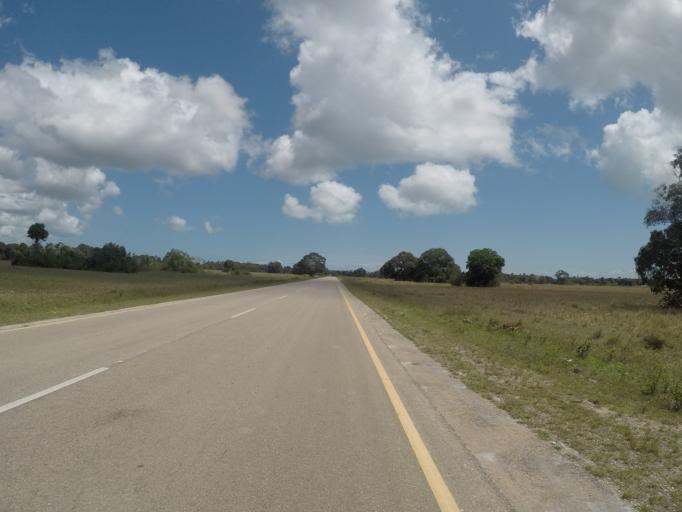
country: TZ
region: Zanzibar Central/South
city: Koani
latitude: -6.2212
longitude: 39.3626
